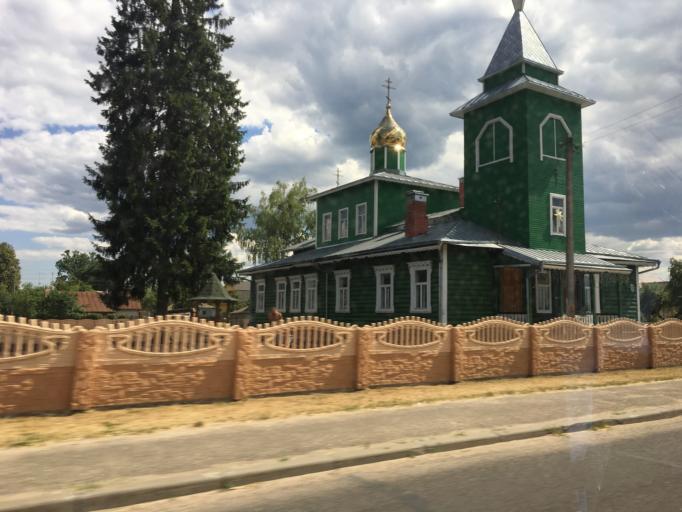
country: LT
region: Alytaus apskritis
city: Druskininkai
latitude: 53.8894
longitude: 24.1391
